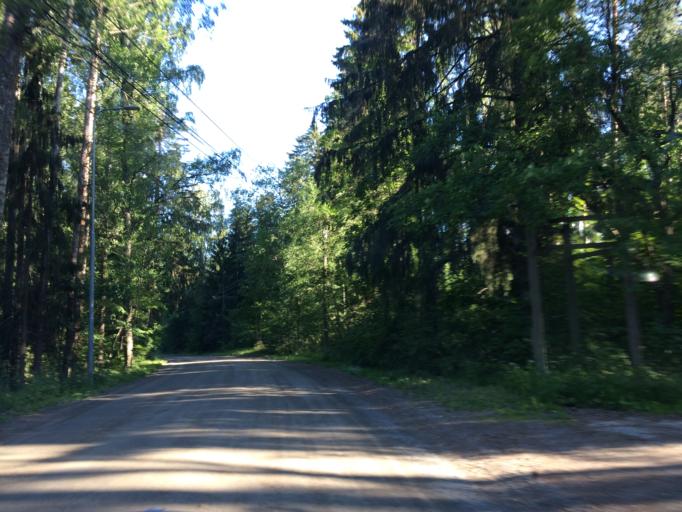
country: FI
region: Haeme
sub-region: Haemeenlinna
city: Haemeenlinna
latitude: 60.9955
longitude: 24.5033
